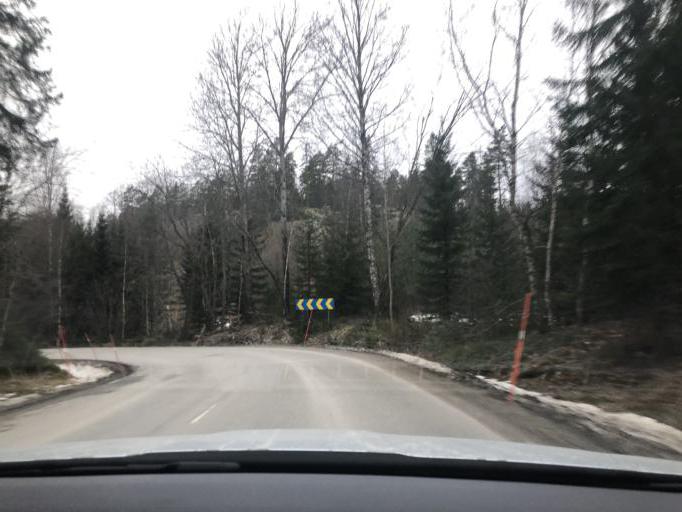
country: SE
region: Stockholm
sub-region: Botkyrka Kommun
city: Tullinge
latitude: 59.1686
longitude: 17.9070
